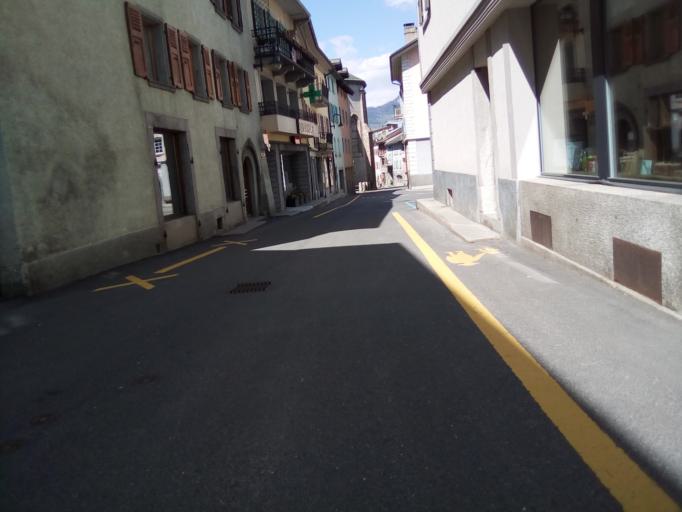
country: CH
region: Valais
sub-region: Entremont District
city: Orsieres
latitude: 46.0302
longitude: 7.1463
